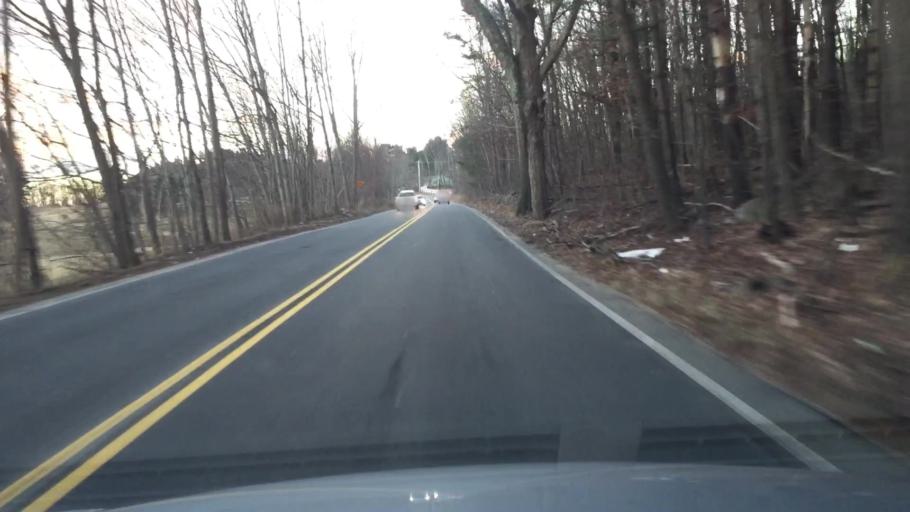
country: US
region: Massachusetts
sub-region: Worcester County
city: Sterling
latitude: 42.4257
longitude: -71.8088
